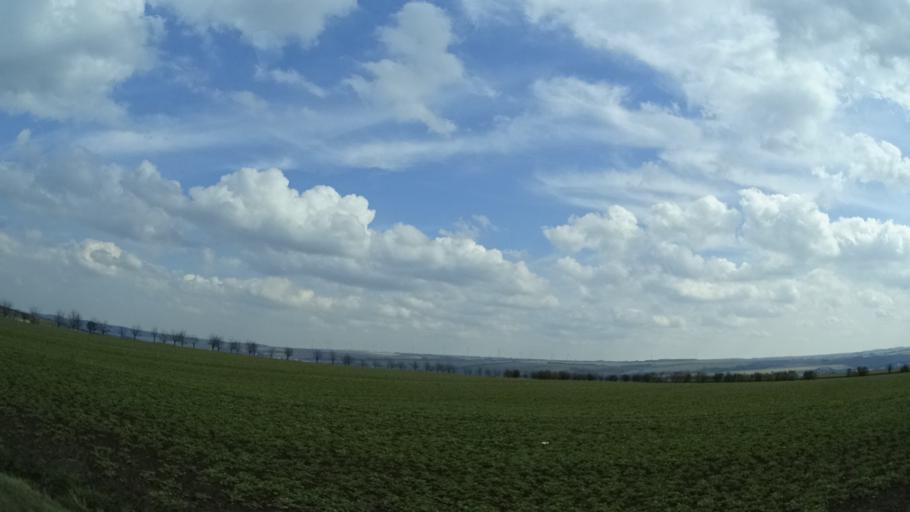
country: DE
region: Thuringia
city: Mattstedt
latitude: 51.0703
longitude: 11.5296
